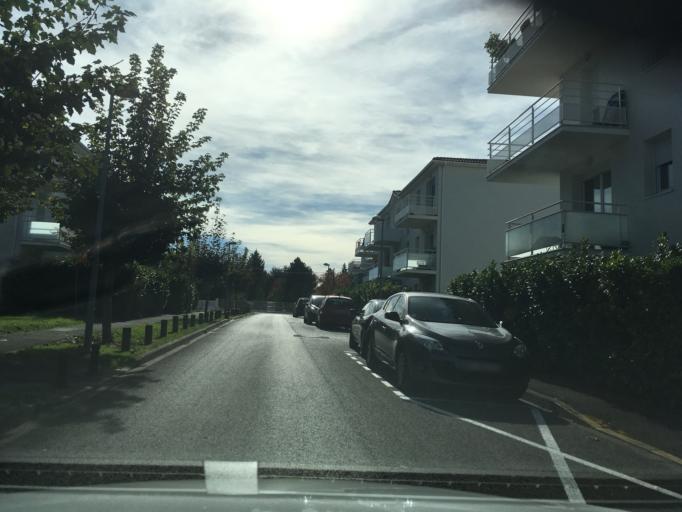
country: FR
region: Aquitaine
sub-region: Departement des Pyrenees-Atlantiques
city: Pau
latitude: 43.3216
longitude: -0.3537
